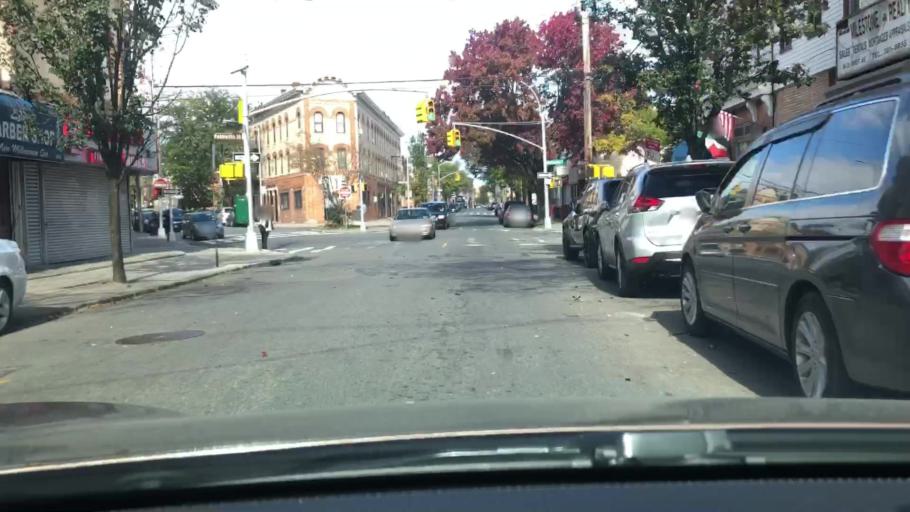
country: US
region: New York
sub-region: Kings County
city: East New York
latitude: 40.7069
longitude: -73.9030
